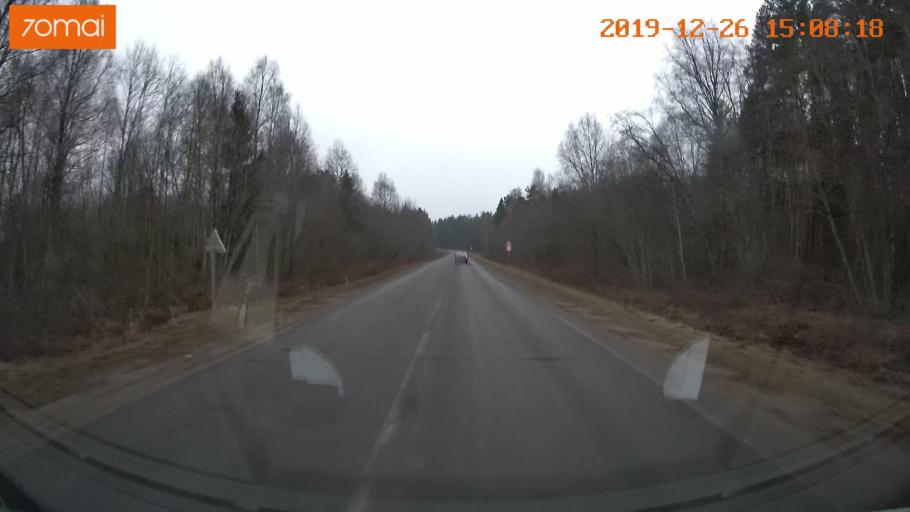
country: RU
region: Jaroslavl
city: Rybinsk
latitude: 58.1611
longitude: 38.8389
